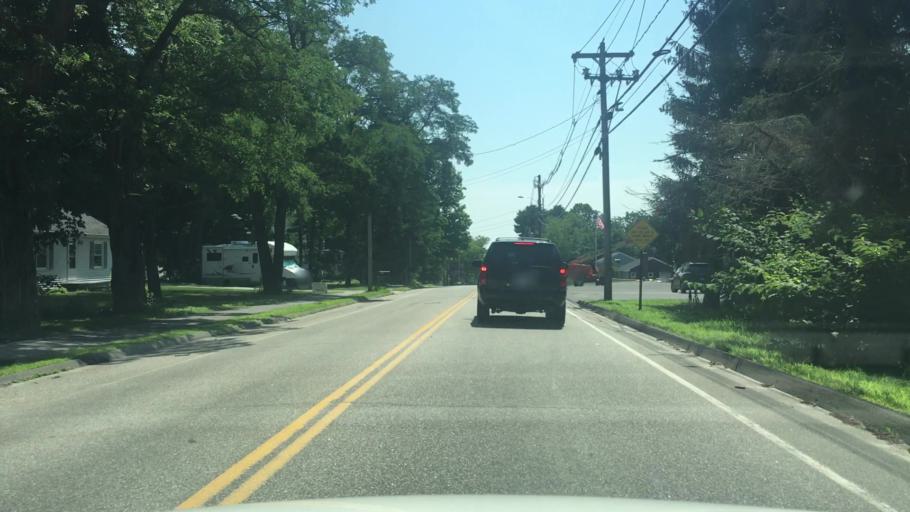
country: US
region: Maine
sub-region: Cumberland County
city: Cumberland Center
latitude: 43.7961
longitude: -70.2577
